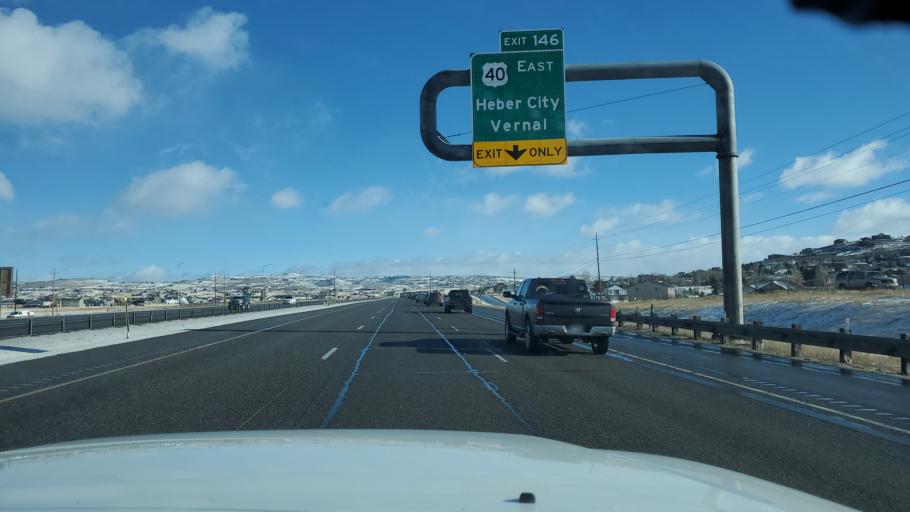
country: US
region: Utah
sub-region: Summit County
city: Snyderville
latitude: 40.7230
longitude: -111.5131
